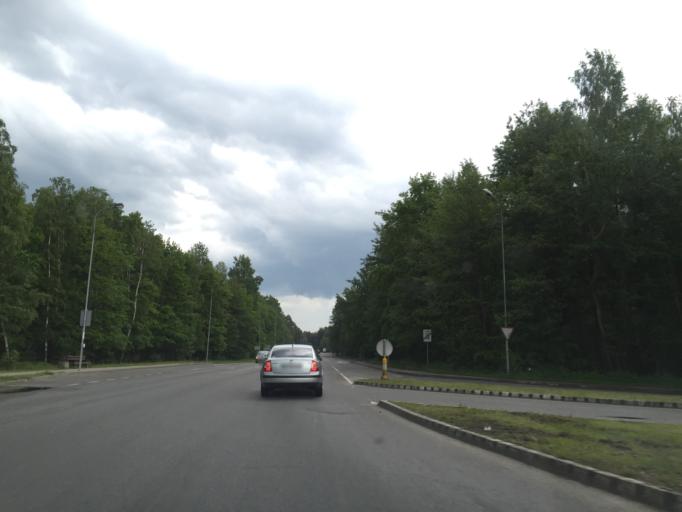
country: LT
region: Klaipedos apskritis
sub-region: Klaipeda
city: Klaipeda
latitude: 55.7376
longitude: 21.0954
